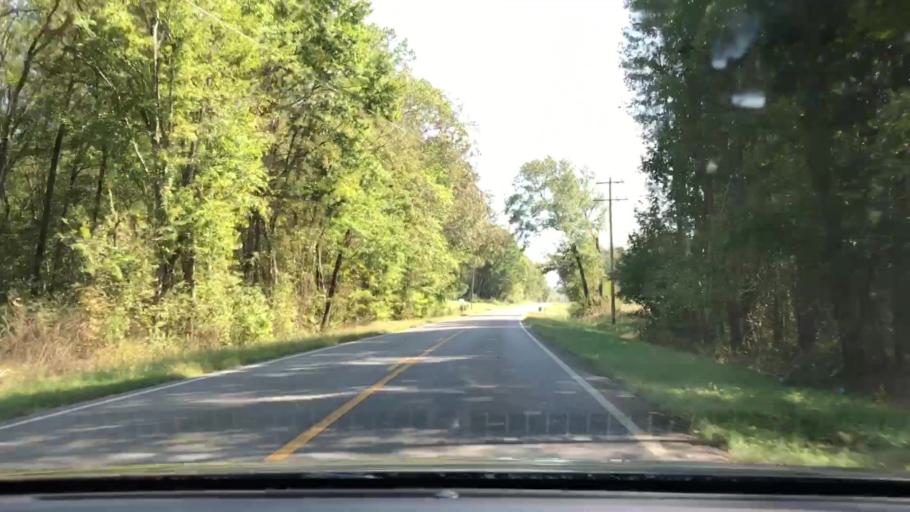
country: US
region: Kentucky
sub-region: Marshall County
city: Benton
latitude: 36.7648
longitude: -88.2465
